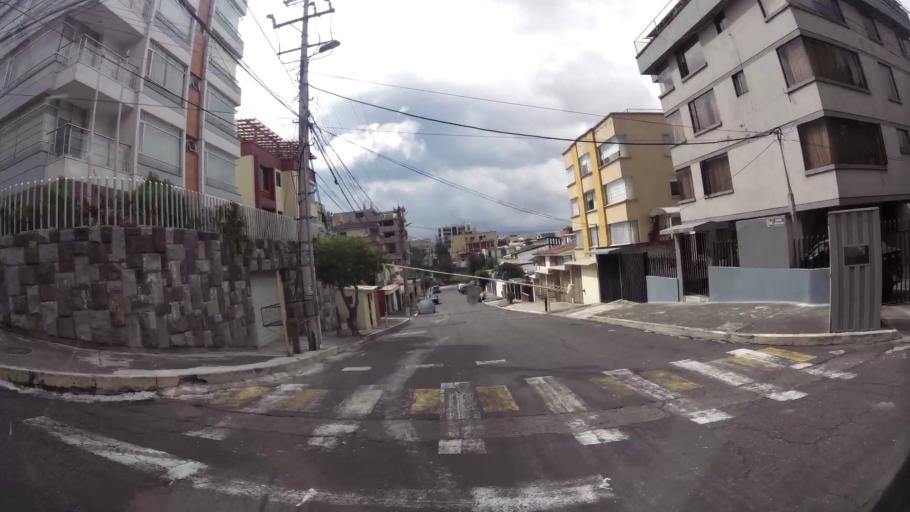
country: EC
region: Pichincha
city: Quito
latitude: -0.1585
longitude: -78.4929
